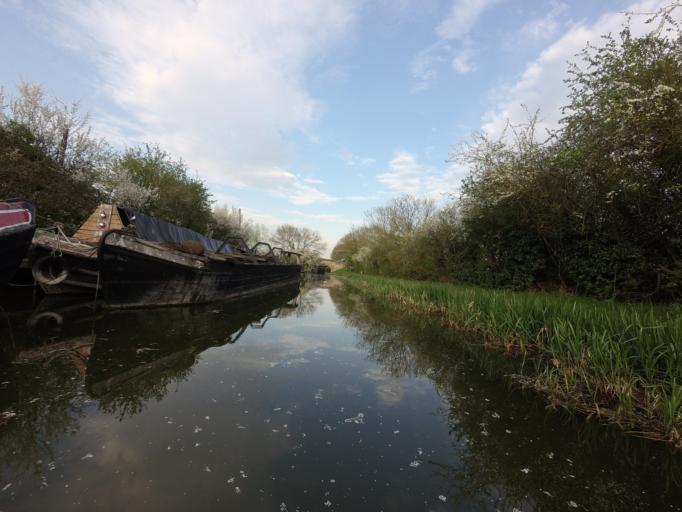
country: GB
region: England
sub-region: Buckinghamshire
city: Aston Clinton
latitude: 51.8176
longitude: -0.7131
